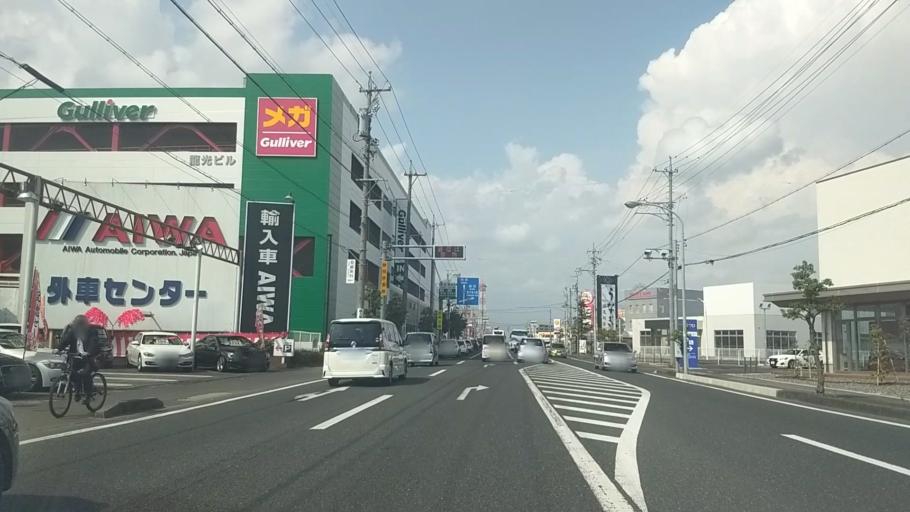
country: JP
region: Shizuoka
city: Hamamatsu
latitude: 34.7194
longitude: 137.7638
